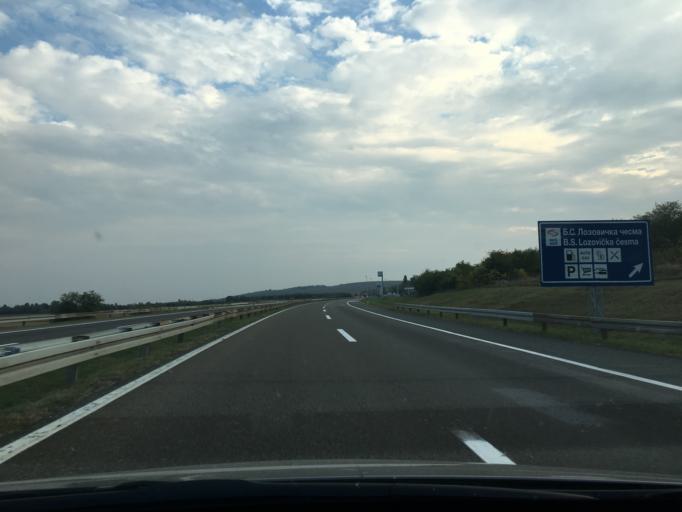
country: RS
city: Lugavcina
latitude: 44.4735
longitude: 21.0387
